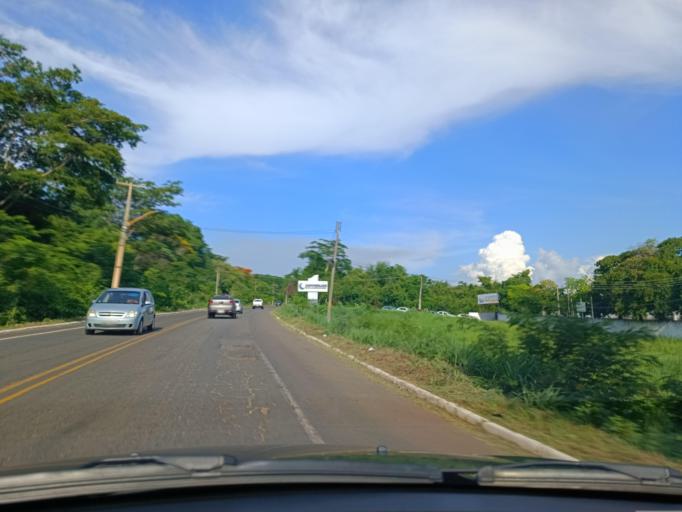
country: BR
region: Piaui
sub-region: Teresina
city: Teresina
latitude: -5.0842
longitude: -42.7545
